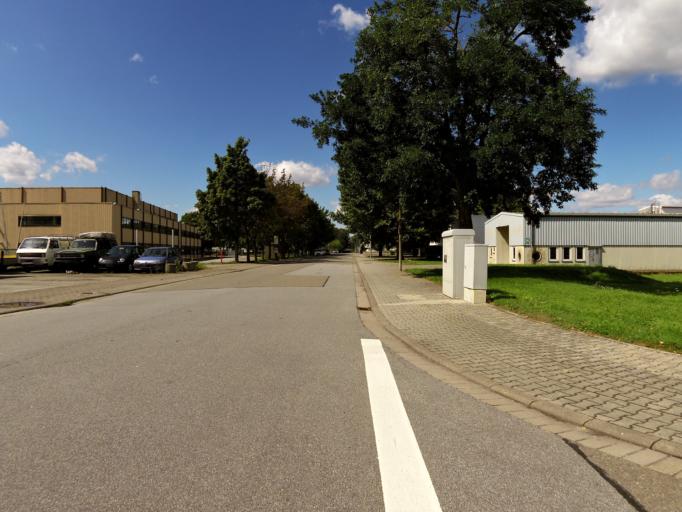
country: DE
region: Hesse
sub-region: Regierungsbezirk Darmstadt
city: Heppenheim an der Bergstrasse
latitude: 49.6426
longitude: 8.6146
